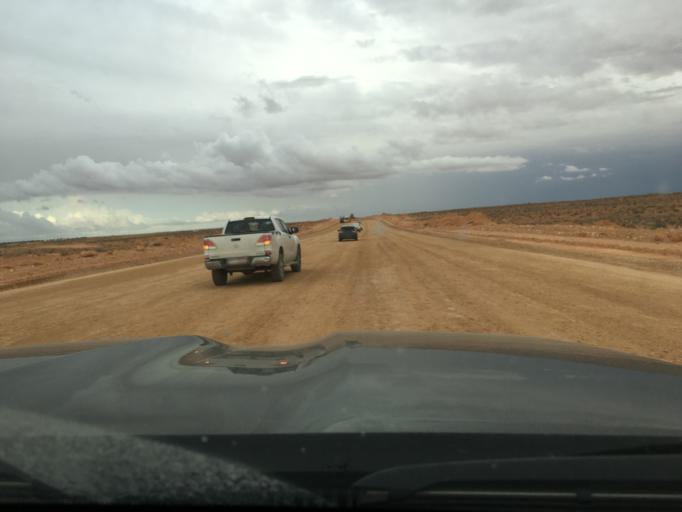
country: TN
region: Madanin
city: Medenine
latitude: 33.2617
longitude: 10.5776
